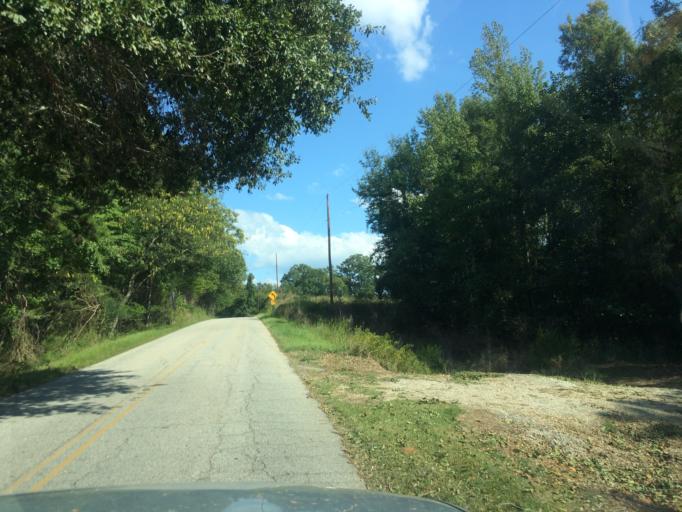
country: US
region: South Carolina
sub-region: Greenwood County
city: Ware Shoals
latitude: 34.4346
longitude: -82.2622
